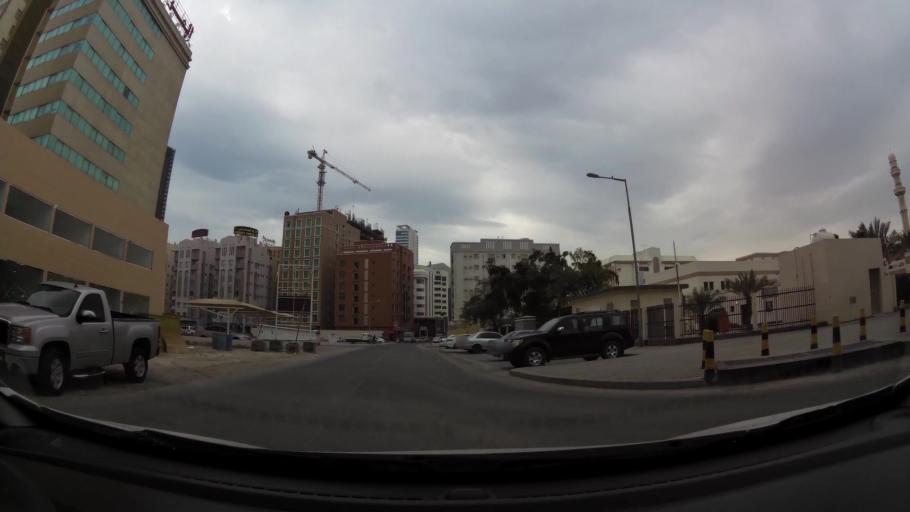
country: BH
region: Manama
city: Manama
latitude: 26.2359
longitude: 50.5949
